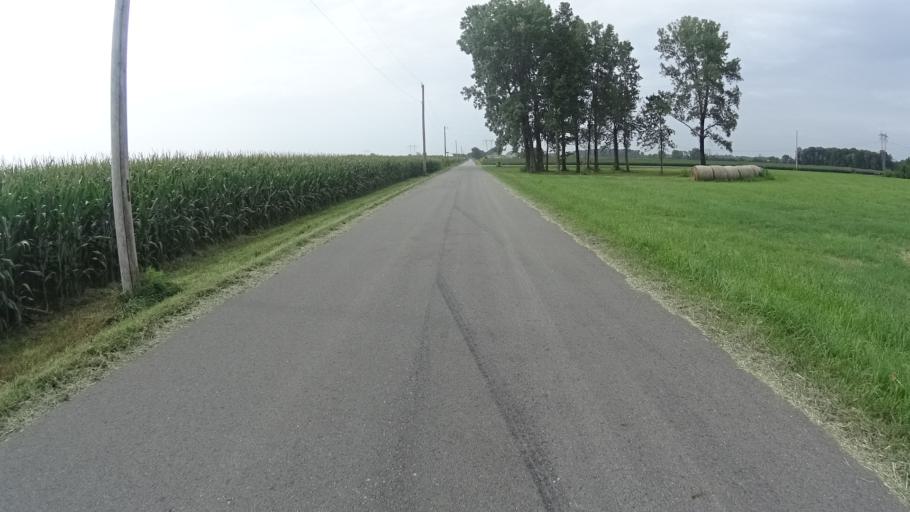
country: US
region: Indiana
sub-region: Madison County
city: Ingalls
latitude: 40.0036
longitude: -85.8149
